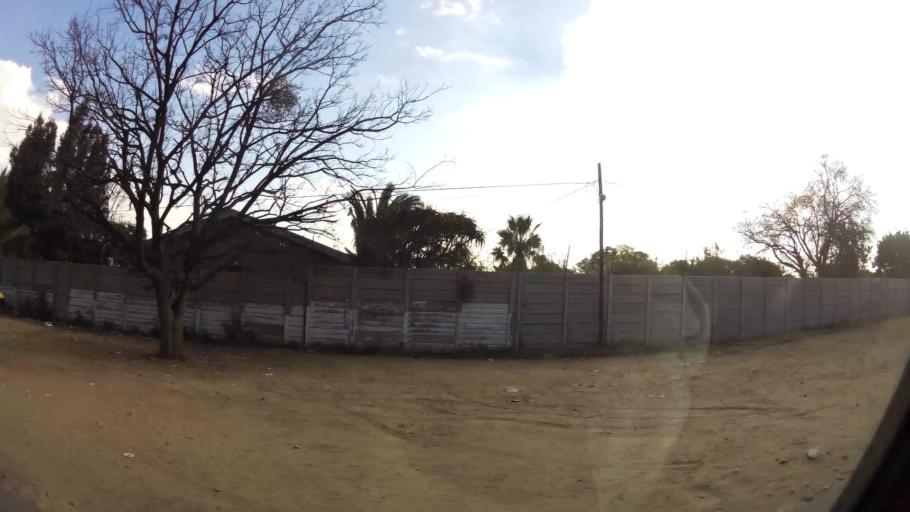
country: ZA
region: Gauteng
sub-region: City of Johannesburg Metropolitan Municipality
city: Midrand
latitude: -26.0039
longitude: 28.1253
